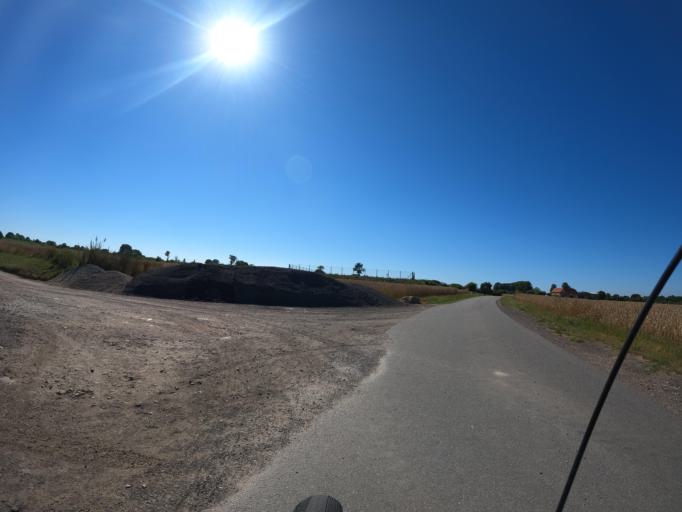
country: DE
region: Schleswig-Holstein
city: Steinberg
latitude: 54.7764
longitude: 9.7703
